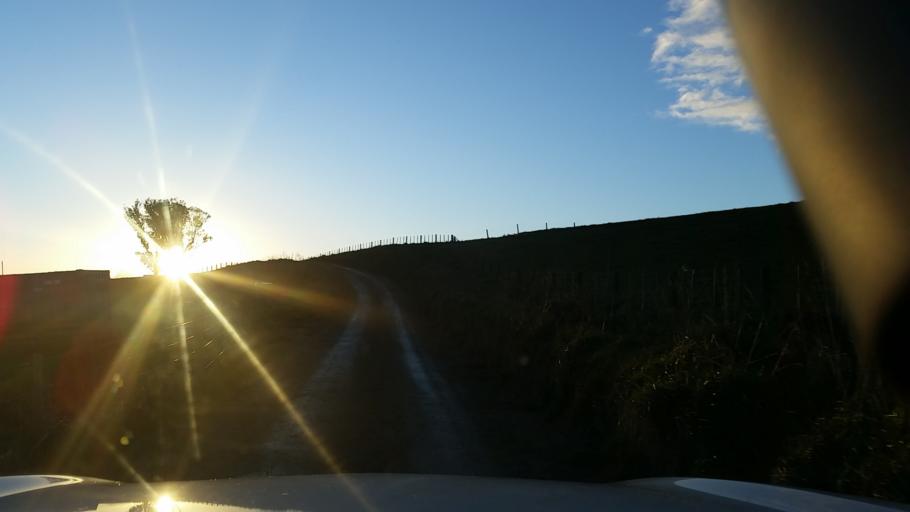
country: NZ
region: Manawatu-Wanganui
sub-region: Wanganui District
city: Wanganui
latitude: -39.7993
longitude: 174.8000
